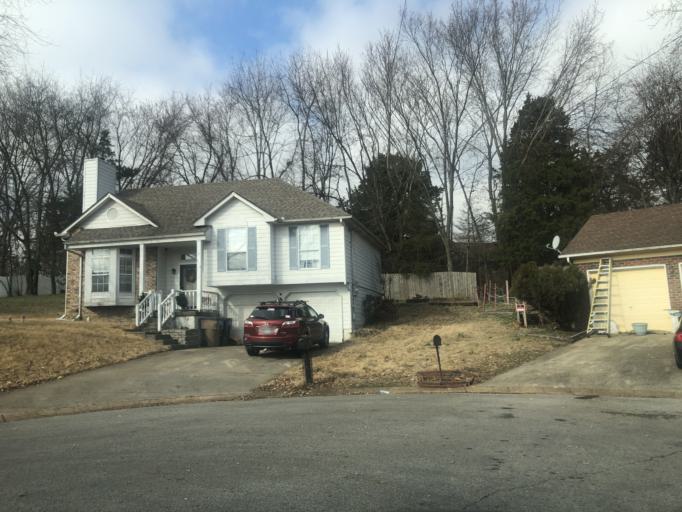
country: US
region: Tennessee
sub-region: Rutherford County
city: La Vergne
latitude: 36.0863
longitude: -86.6526
